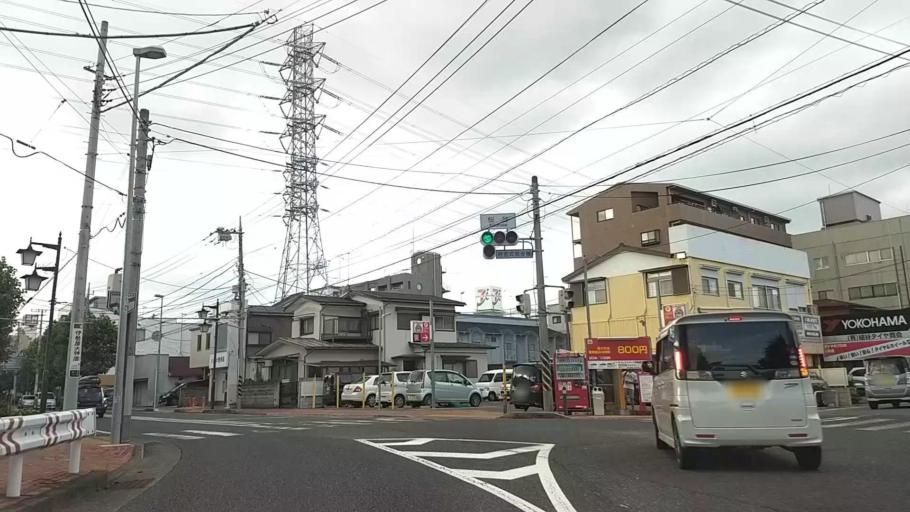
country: JP
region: Kanagawa
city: Isehara
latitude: 35.3925
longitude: 139.3145
